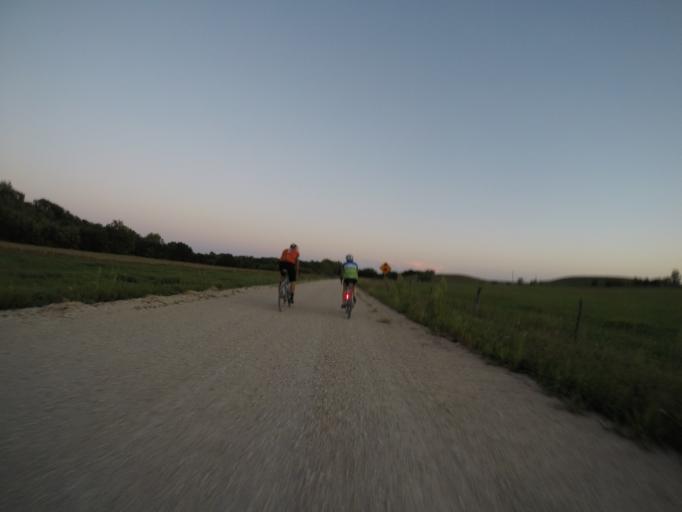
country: US
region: Kansas
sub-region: Riley County
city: Ogden
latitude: 38.9740
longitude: -96.5624
